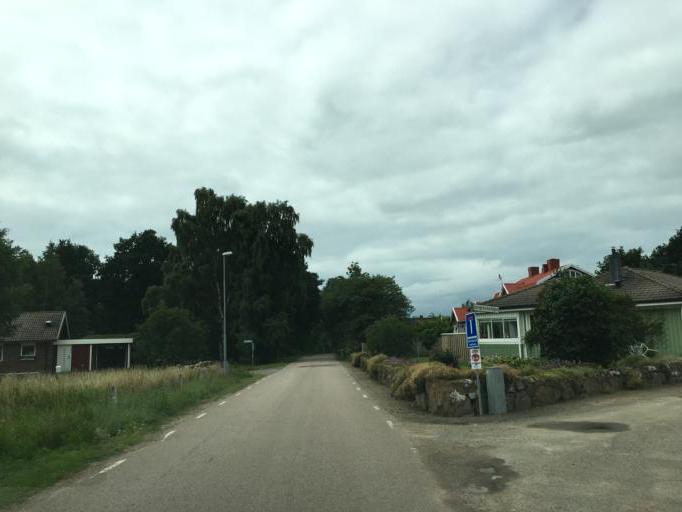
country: SE
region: Skane
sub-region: Angelholms Kommun
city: Vejbystrand
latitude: 56.3243
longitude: 12.7691
